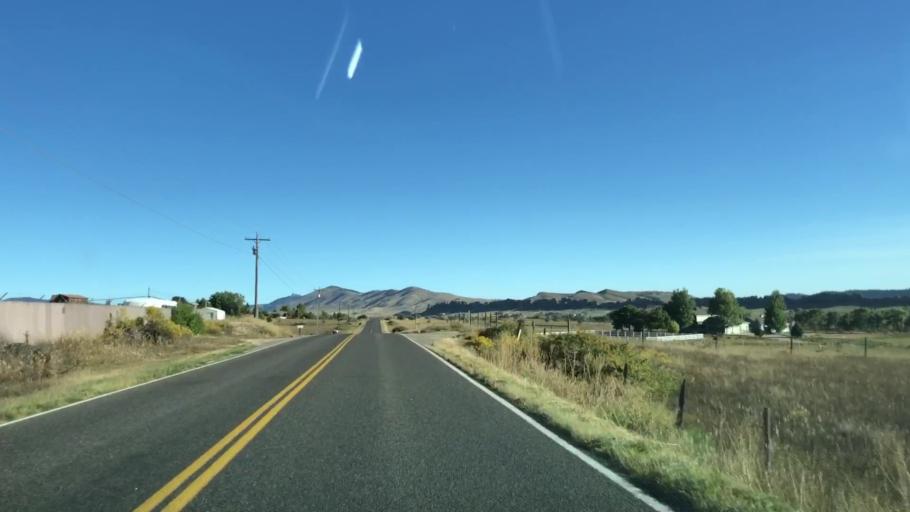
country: US
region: Colorado
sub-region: Larimer County
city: Loveland
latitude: 40.3964
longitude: -105.1683
